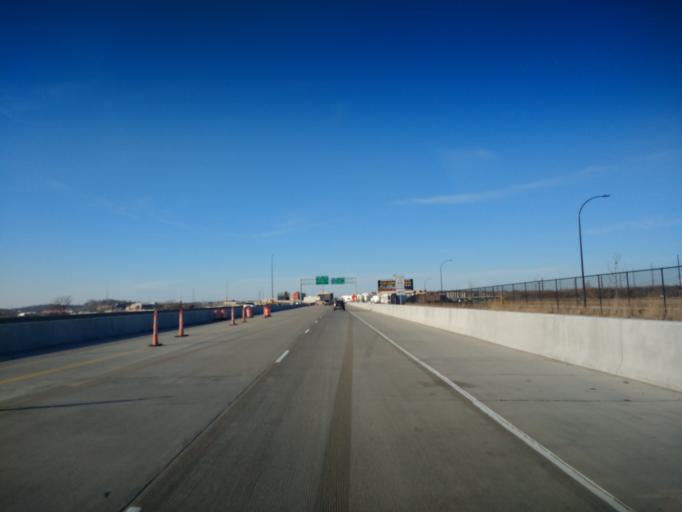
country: US
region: Iowa
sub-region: Woodbury County
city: Sioux City
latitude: 42.4815
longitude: -96.3889
